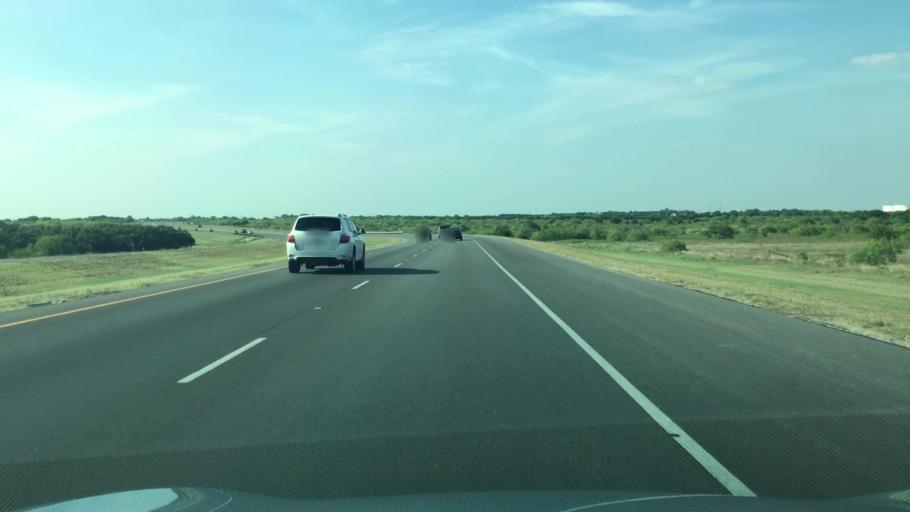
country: US
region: Texas
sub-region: Hays County
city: Kyle
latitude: 30.0348
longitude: -97.8721
